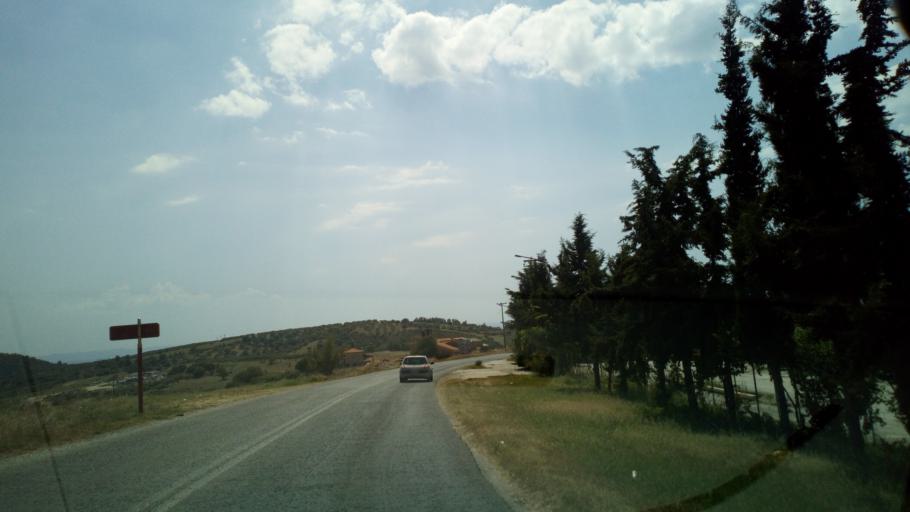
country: GR
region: Central Macedonia
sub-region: Nomos Chalkidikis
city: Nikiti
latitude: 40.2158
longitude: 23.6970
